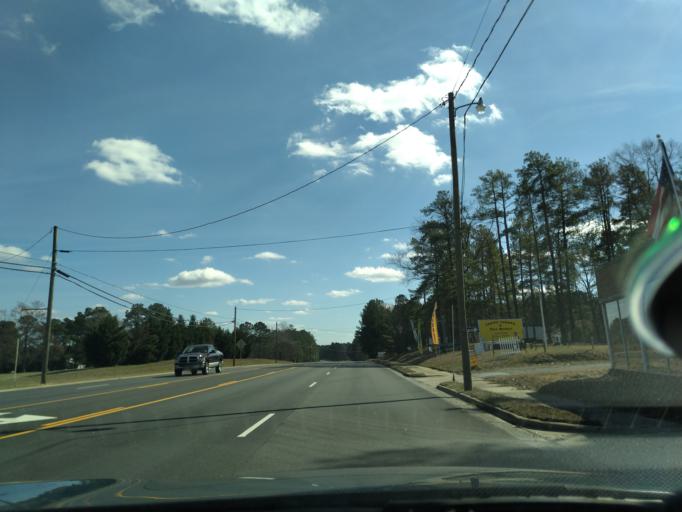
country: US
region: Virginia
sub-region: Nottoway County
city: Crewe
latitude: 37.1664
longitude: -78.1161
